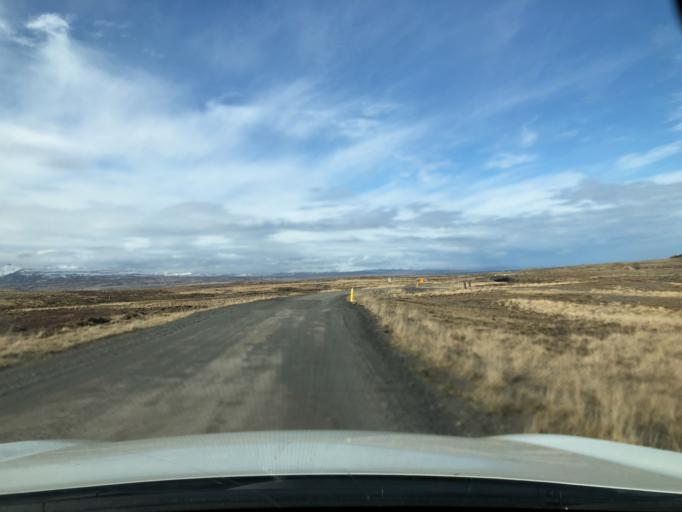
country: IS
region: West
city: Borgarnes
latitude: 65.0525
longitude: -21.6863
